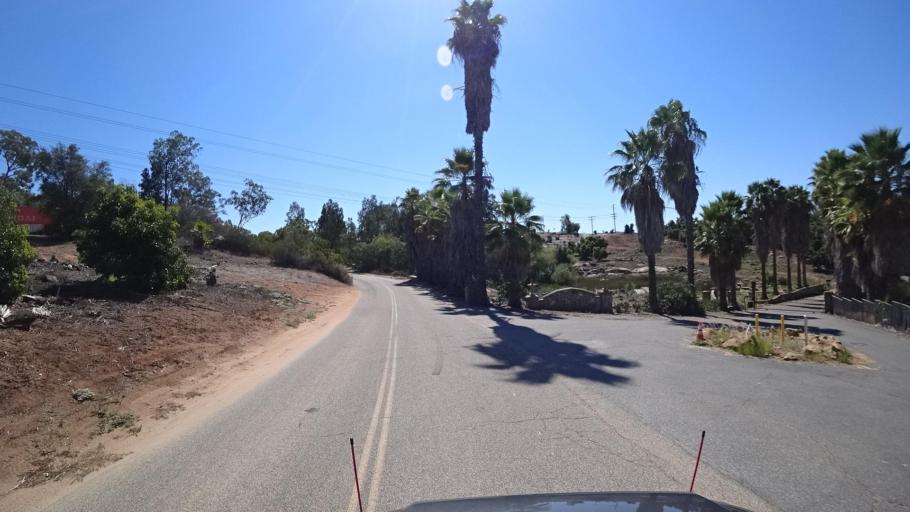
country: US
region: California
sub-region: San Diego County
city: Hidden Meadows
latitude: 33.2407
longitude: -117.0859
